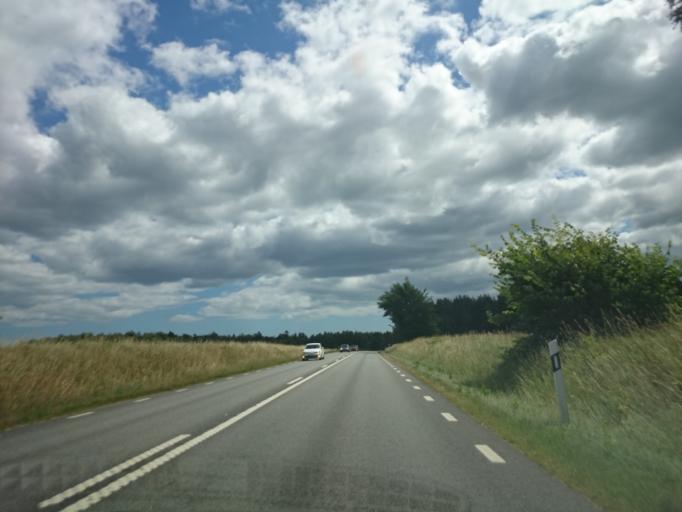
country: SE
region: Skane
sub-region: Kristianstads Kommun
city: Degeberga
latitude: 55.8186
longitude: 14.1256
